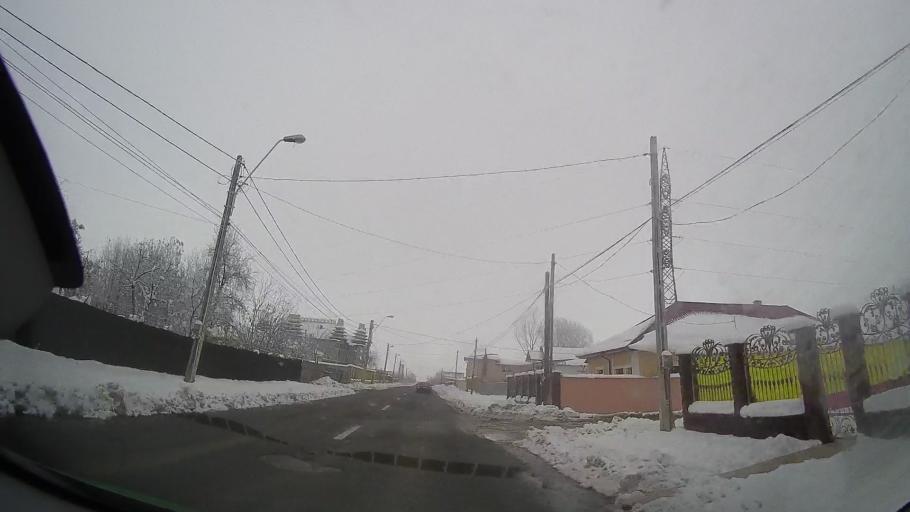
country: RO
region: Neamt
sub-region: Comuna Horia
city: Cotu Vames
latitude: 46.9342
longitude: 26.9432
